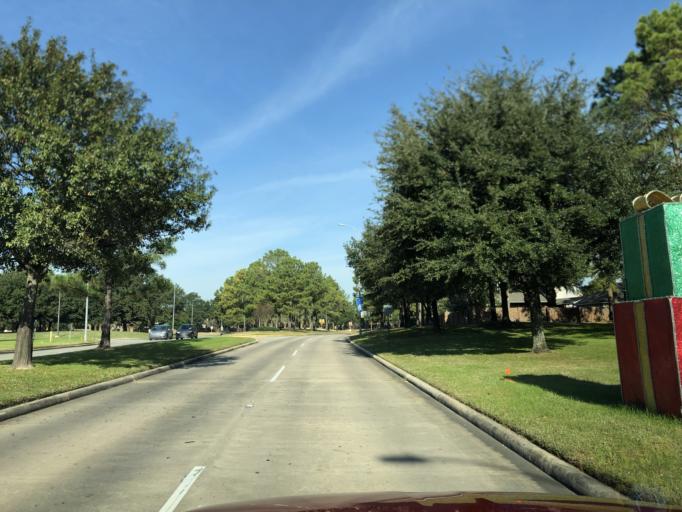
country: US
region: Texas
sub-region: Harris County
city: Tomball
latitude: 30.0277
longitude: -95.5636
